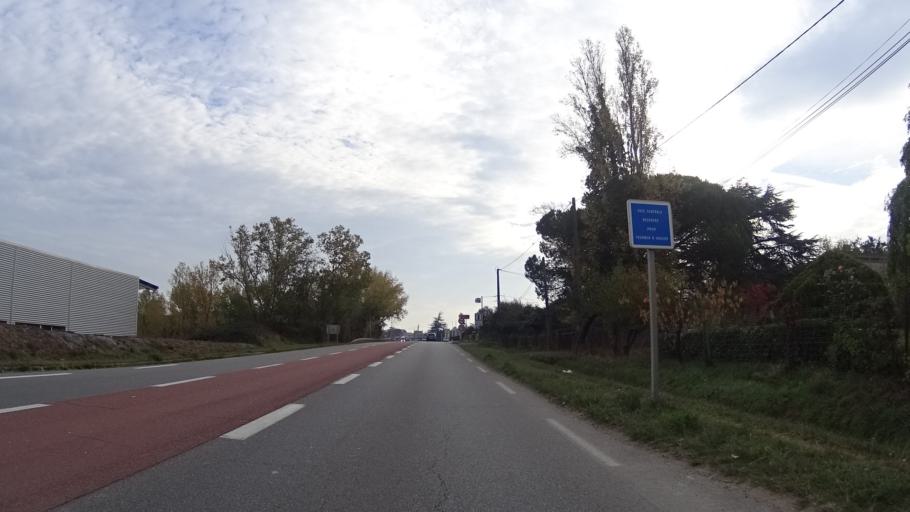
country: FR
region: Aquitaine
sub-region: Departement du Lot-et-Garonne
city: Estillac
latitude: 44.1655
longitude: 0.5941
